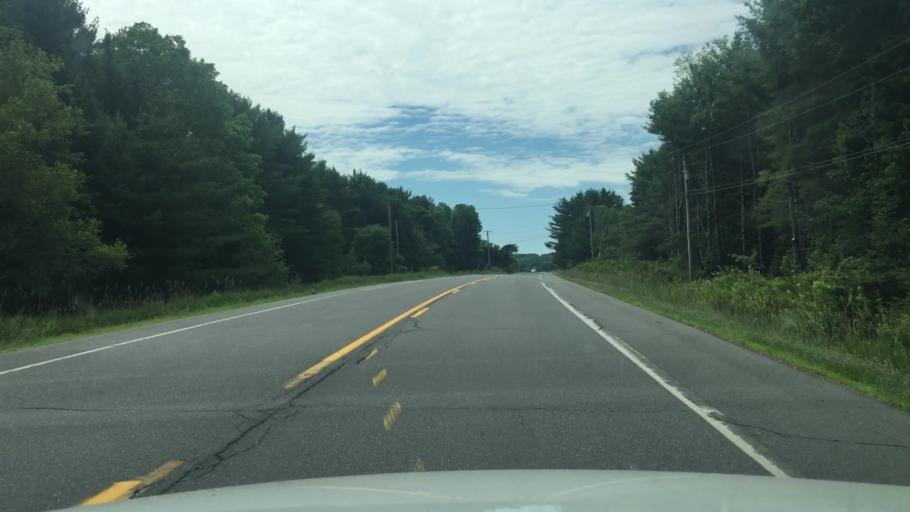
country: US
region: Maine
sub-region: Waldo County
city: Troy
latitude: 44.5895
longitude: -69.2812
